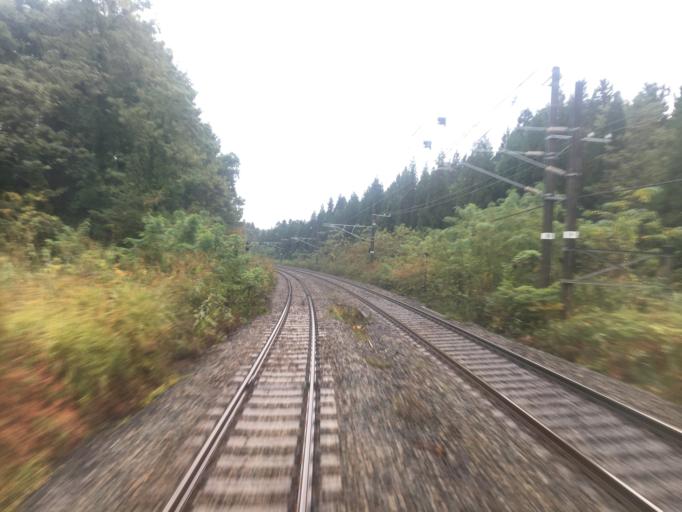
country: JP
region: Yamagata
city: Shinjo
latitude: 38.7333
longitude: 140.3072
